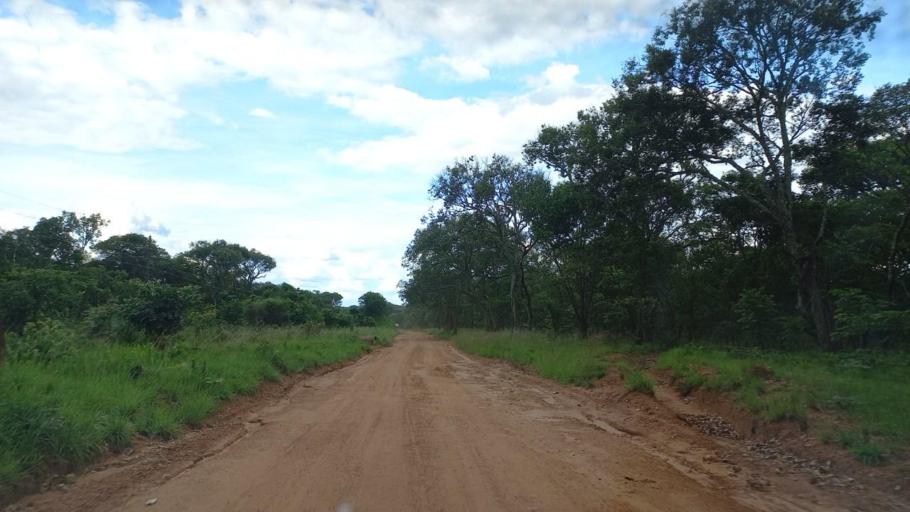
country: ZM
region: North-Western
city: Mwinilunga
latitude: -11.8152
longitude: 24.3655
